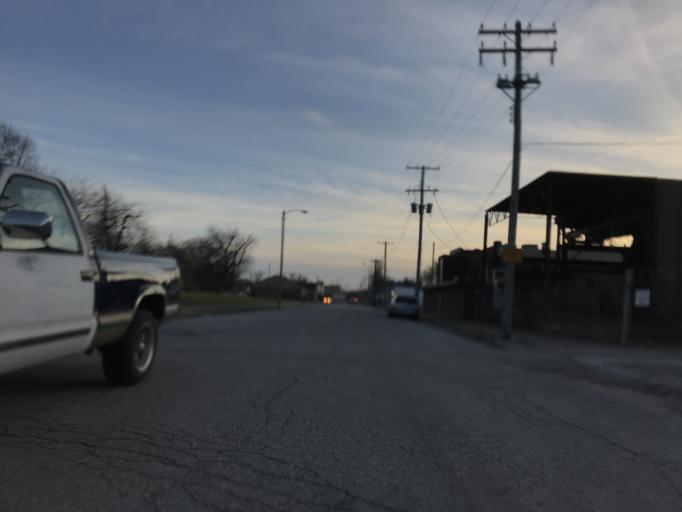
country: US
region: Kentucky
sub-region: Jefferson County
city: Louisville
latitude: 38.2391
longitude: -85.7664
